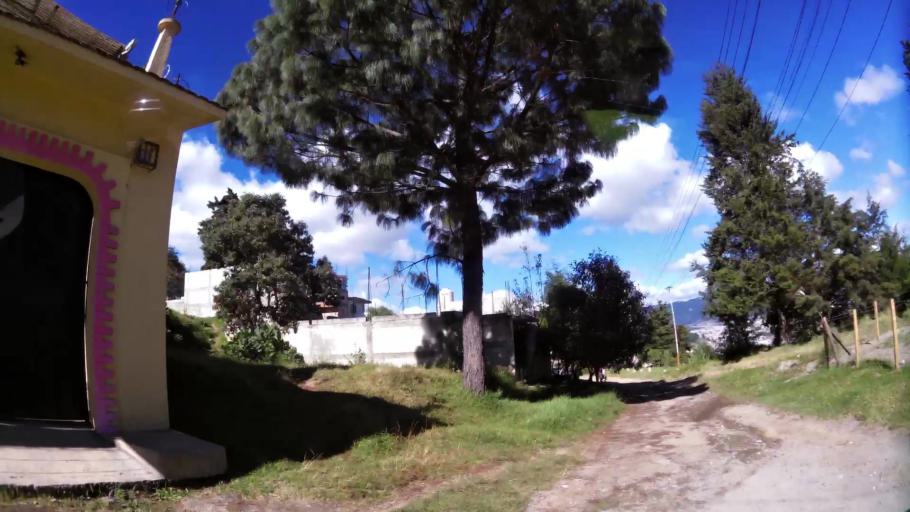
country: GT
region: Quetzaltenango
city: Quetzaltenango
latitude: 14.8350
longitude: -91.5008
